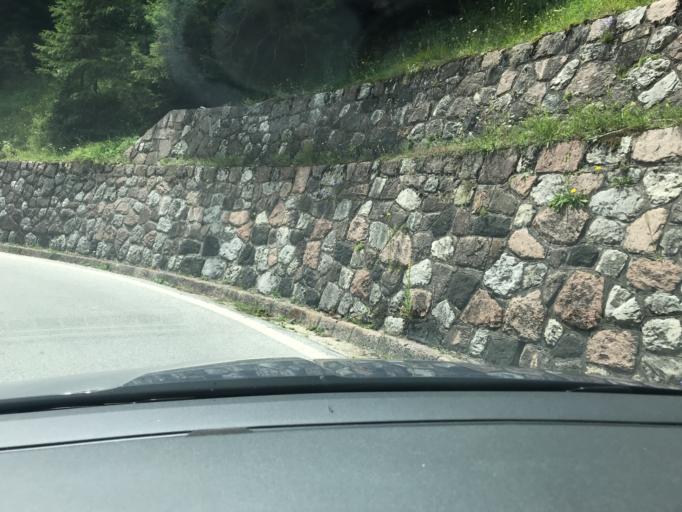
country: IT
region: Trentino-Alto Adige
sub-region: Provincia di Trento
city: Canazei
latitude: 46.4632
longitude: 11.8259
